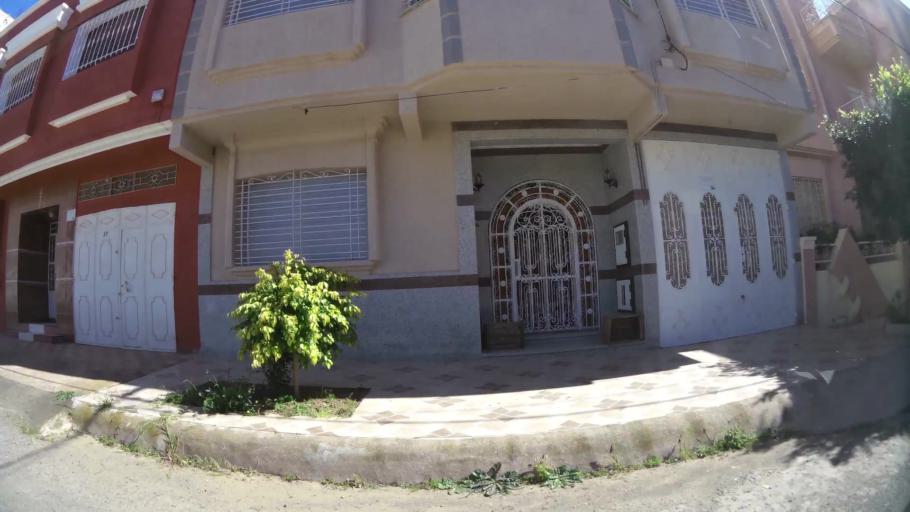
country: MA
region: Oriental
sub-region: Berkane-Taourirt
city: Berkane
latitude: 34.9394
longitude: -2.3277
